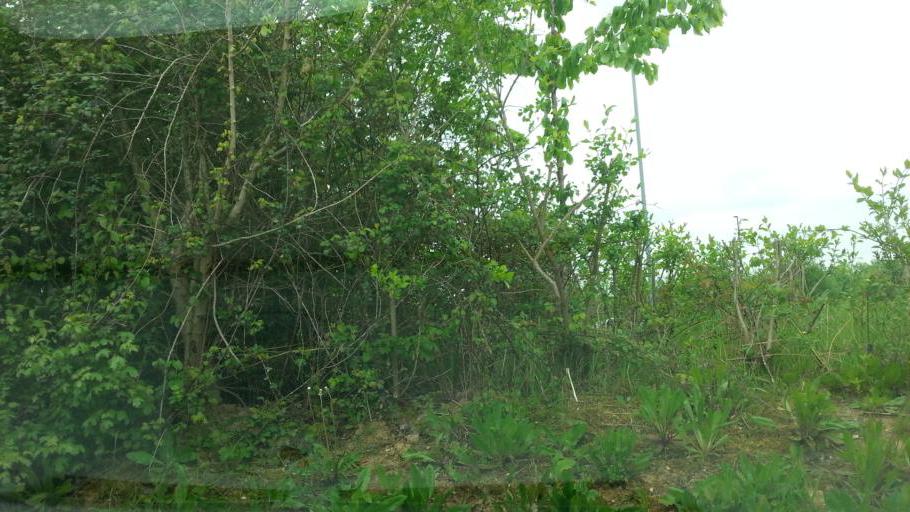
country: GB
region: England
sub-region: Lincolnshire
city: Bourne
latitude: 52.7585
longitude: -0.3928
